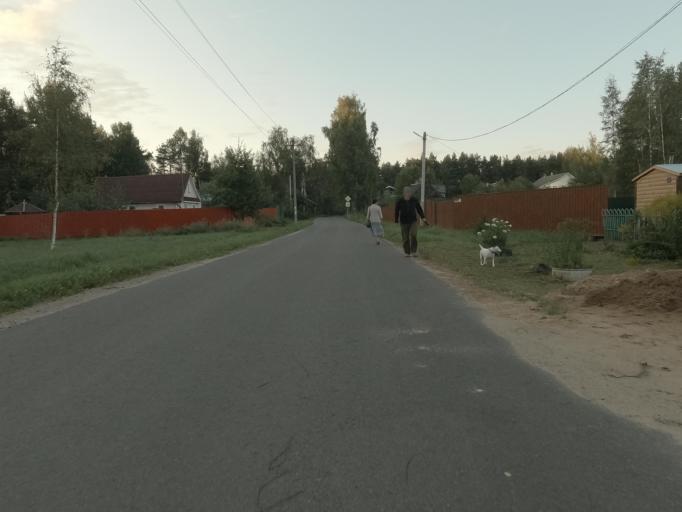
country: RU
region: Leningrad
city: Mga
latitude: 59.7604
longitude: 31.0469
